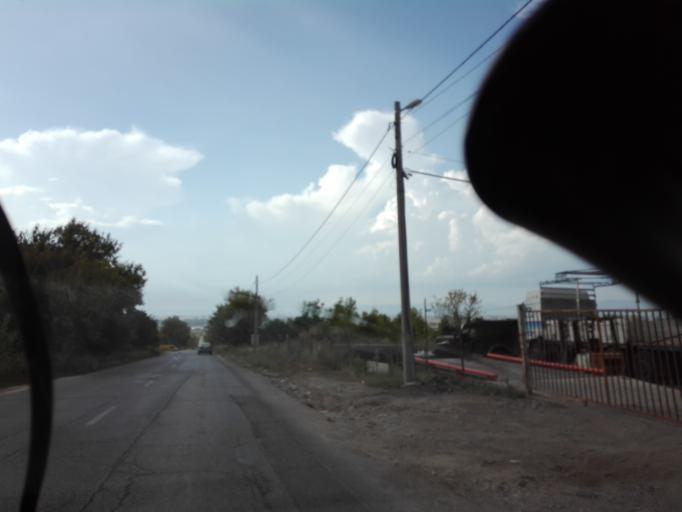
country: BG
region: Sofiya
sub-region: Obshtina Elin Pelin
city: Elin Pelin
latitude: 42.6094
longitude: 23.4667
